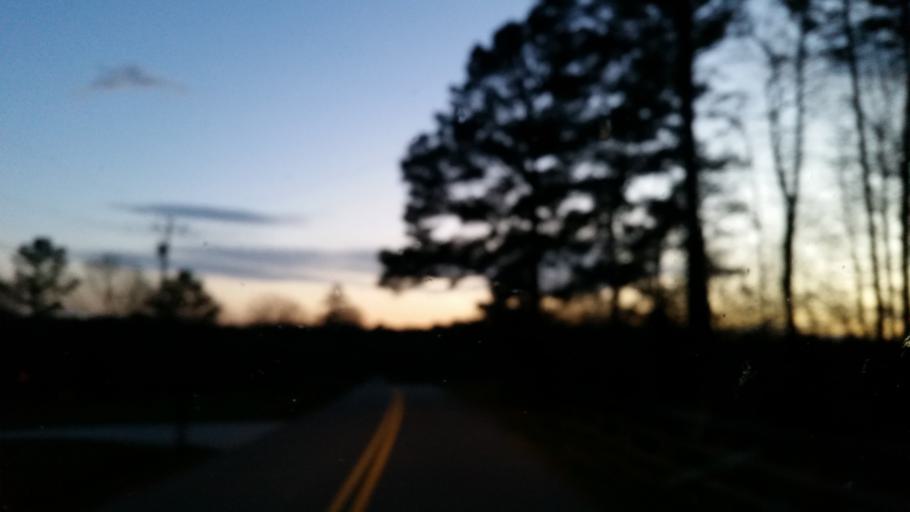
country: US
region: Georgia
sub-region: Cherokee County
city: Ball Ground
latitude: 34.3071
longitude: -84.4366
